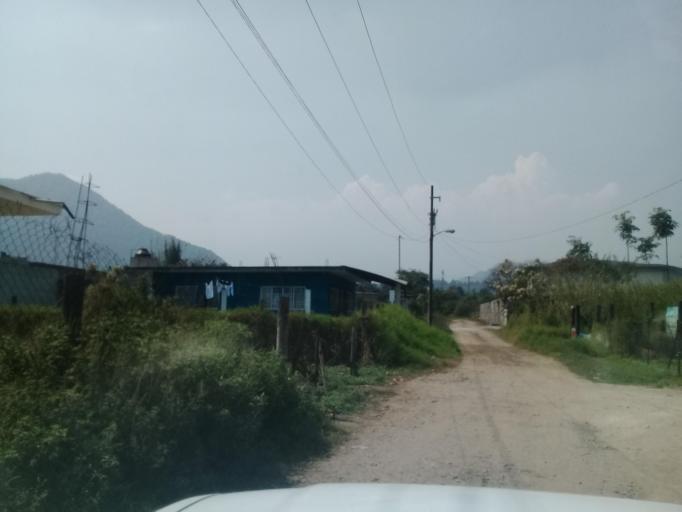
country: MX
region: Veracruz
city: Ixtac Zoquitlan
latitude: 18.8720
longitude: -97.0597
